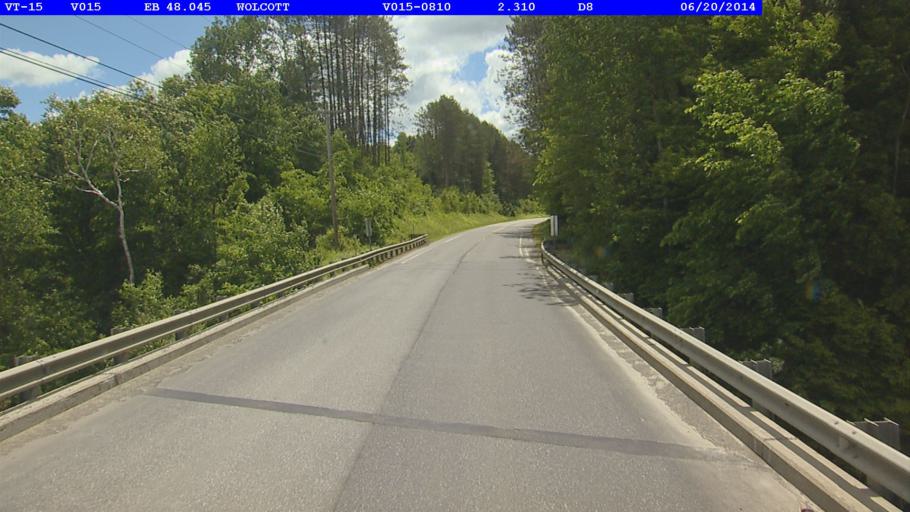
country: US
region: Vermont
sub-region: Lamoille County
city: Morrisville
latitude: 44.5615
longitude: -72.4901
